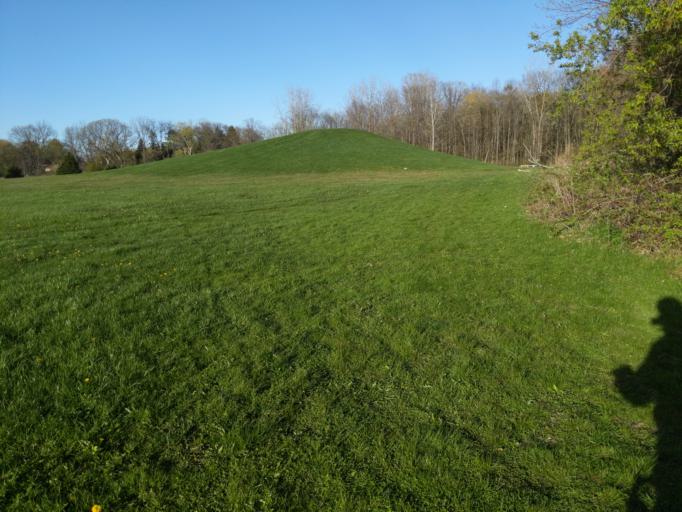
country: US
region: Michigan
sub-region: Clinton County
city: Saint Johns
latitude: 42.9962
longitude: -84.5741
